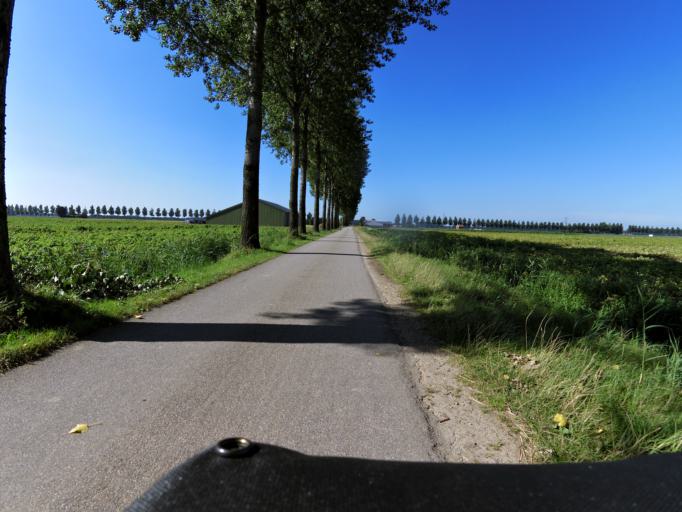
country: NL
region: South Holland
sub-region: Gemeente Dordrecht
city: Dordrecht
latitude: 51.7627
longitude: 4.7181
